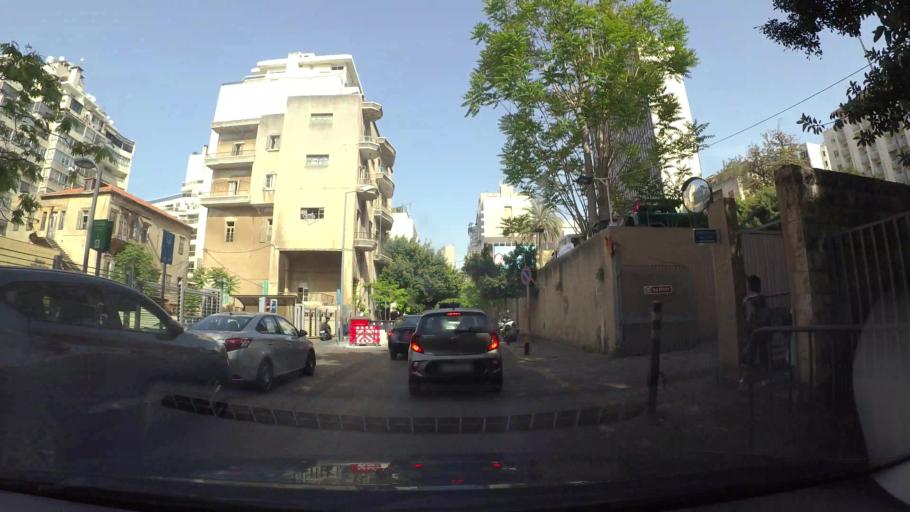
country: LB
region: Beyrouth
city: Ra's Bayrut
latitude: 33.8988
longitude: 35.4859
